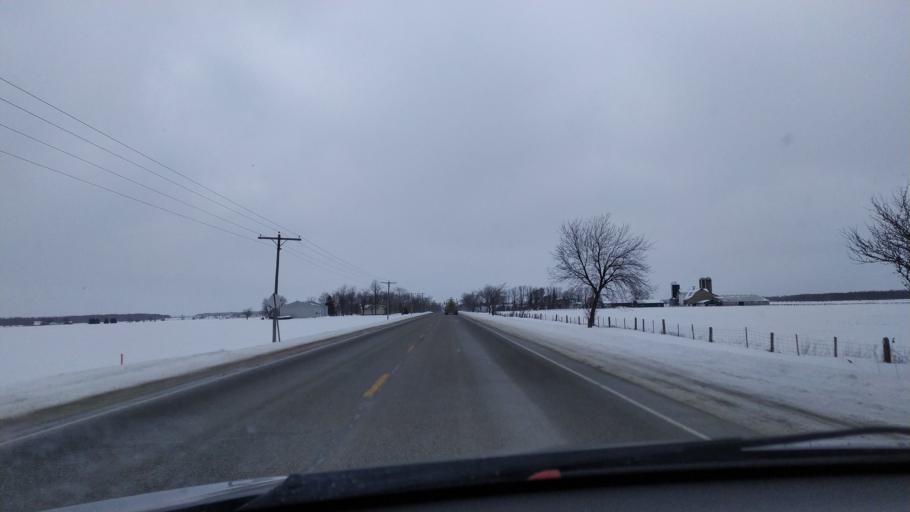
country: CA
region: Ontario
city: North Perth
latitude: 43.5824
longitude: -80.8606
